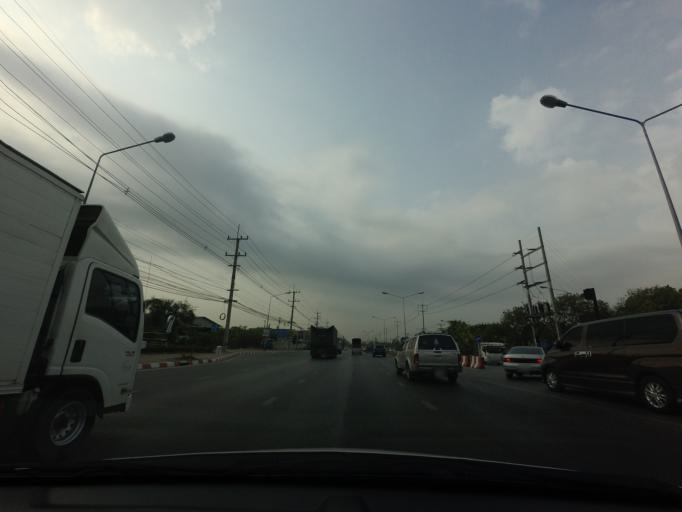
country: TH
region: Bangkok
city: Thawi Watthana
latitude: 13.7677
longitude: 100.3285
